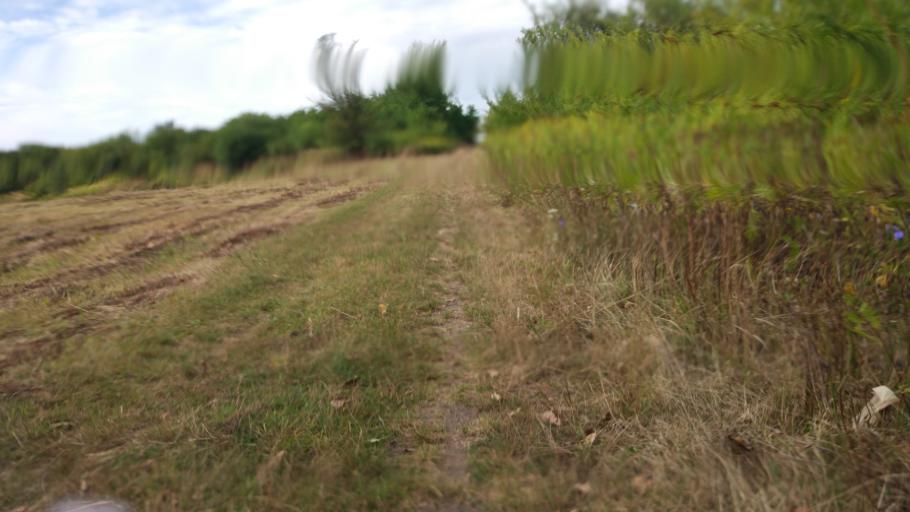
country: PL
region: Masovian Voivodeship
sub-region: Plock
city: Plock
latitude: 52.5283
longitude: 19.7444
